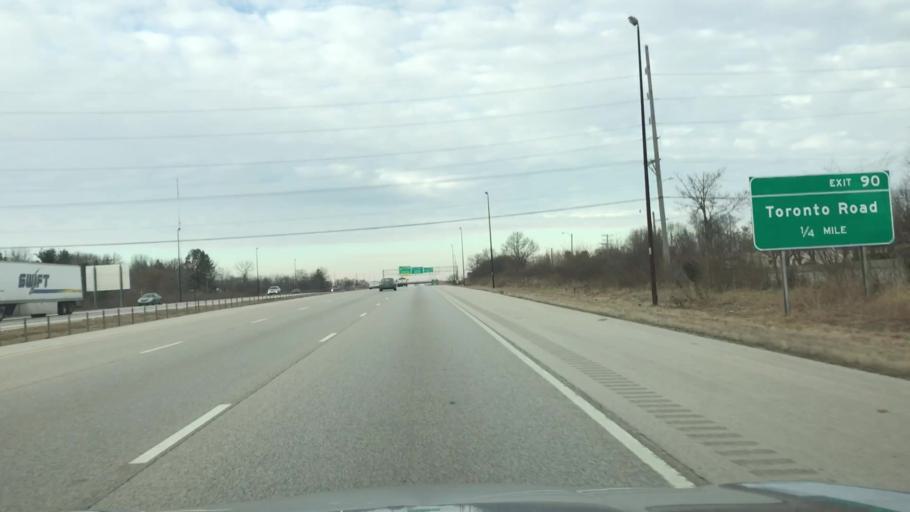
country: US
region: Illinois
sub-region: Sangamon County
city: Southern View
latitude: 39.7060
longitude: -89.6435
